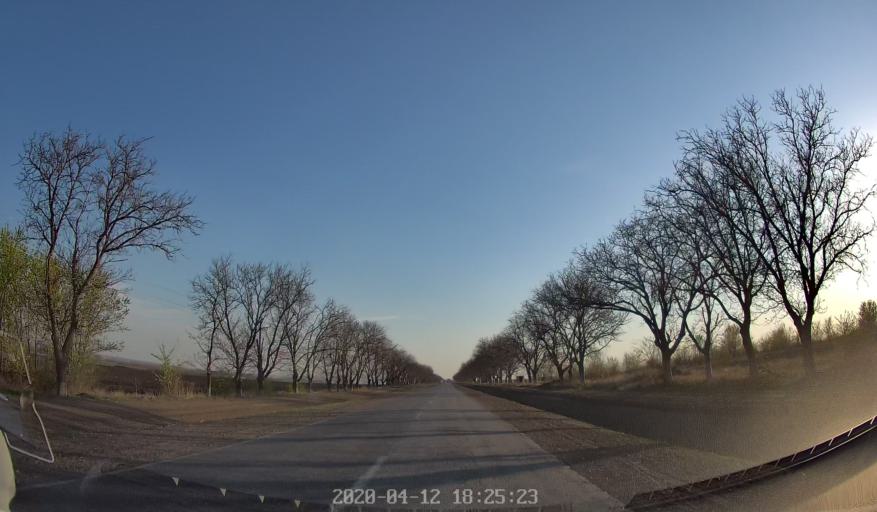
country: MD
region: Criuleni
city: Criuleni
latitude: 47.1843
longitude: 29.1401
